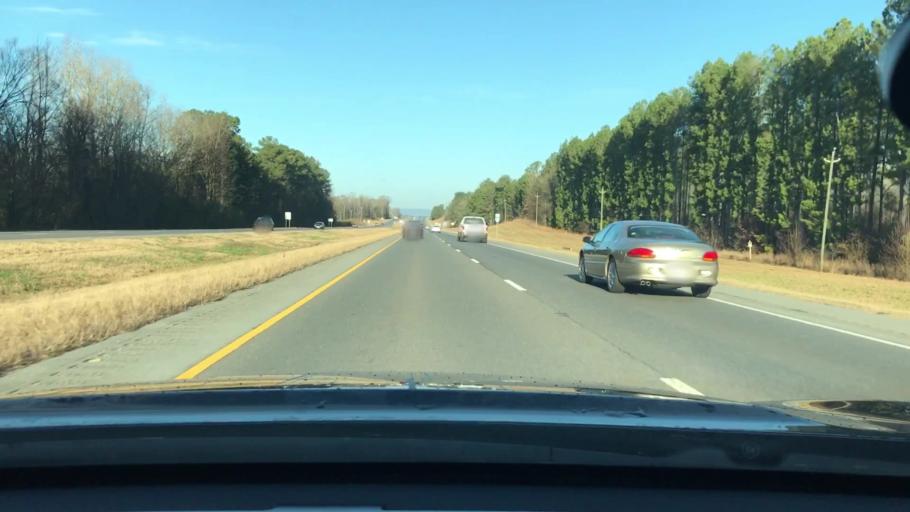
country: US
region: Alabama
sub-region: Talladega County
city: Childersburg
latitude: 33.3077
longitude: -86.3796
